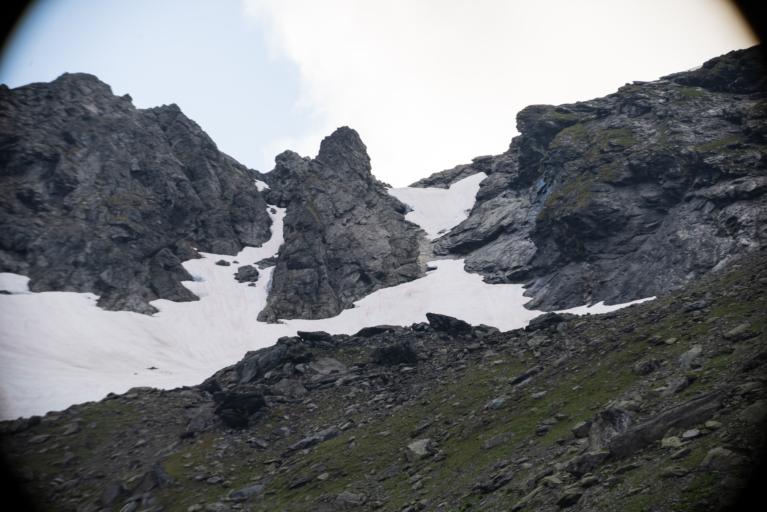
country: RU
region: Komi Republic
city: Synya
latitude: 64.8278
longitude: 59.3102
